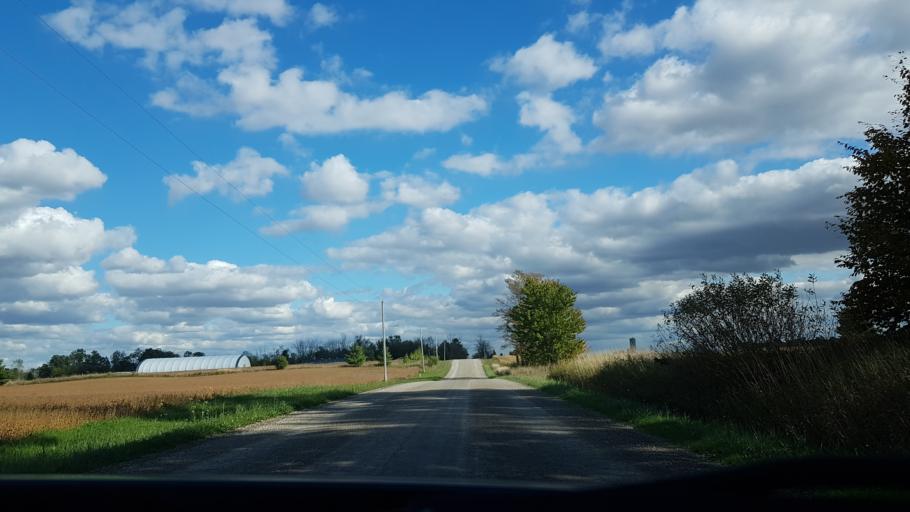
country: CA
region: Ontario
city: South Huron
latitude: 43.1120
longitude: -81.6437
